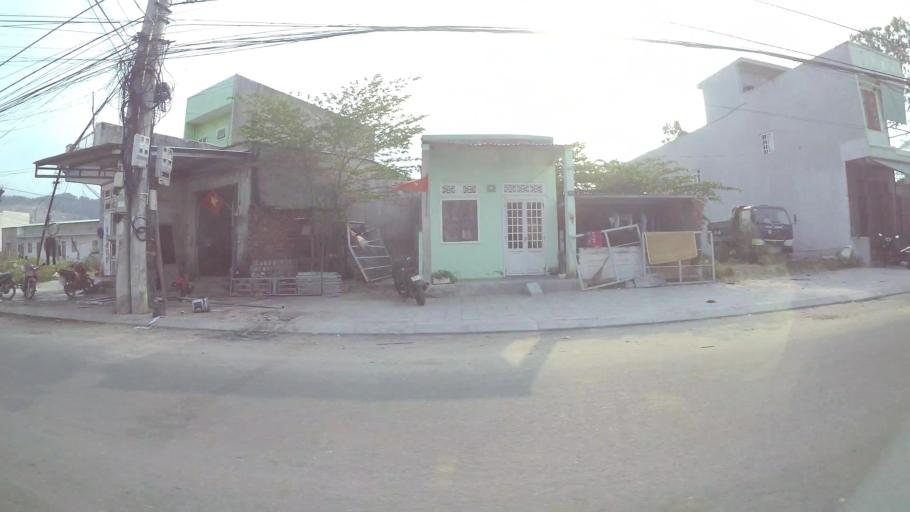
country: VN
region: Da Nang
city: Lien Chieu
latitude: 16.0503
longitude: 108.1550
